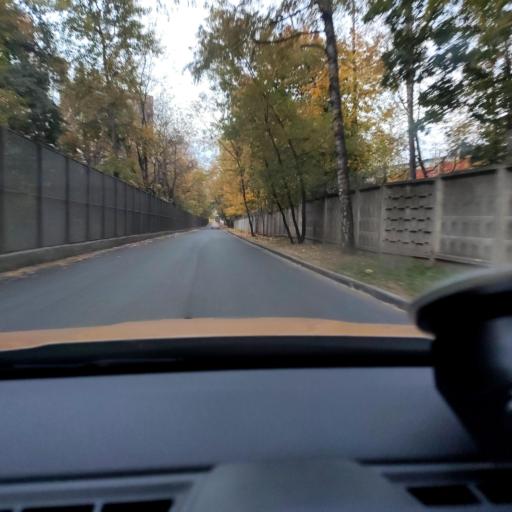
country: RU
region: Moscow
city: Vatutino
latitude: 55.8609
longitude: 37.6996
